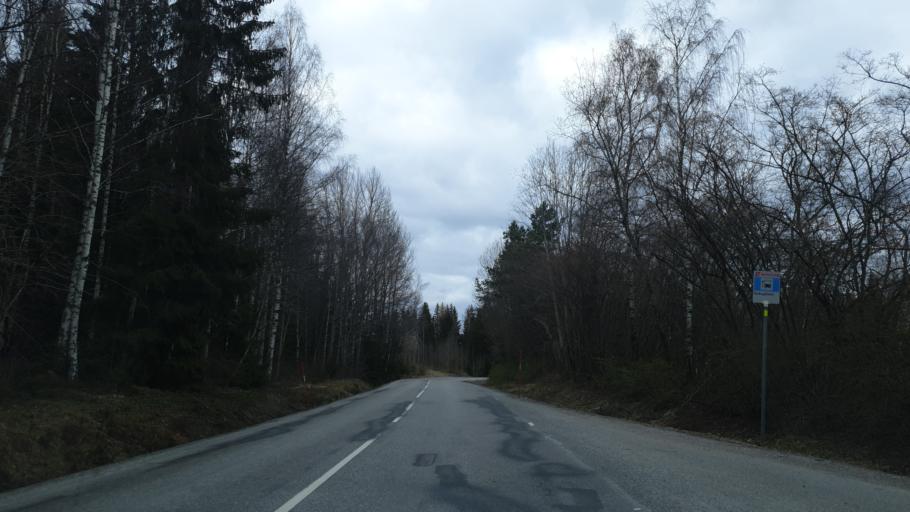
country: SE
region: OErebro
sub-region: Nora Kommun
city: Nora
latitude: 59.5452
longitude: 15.0297
